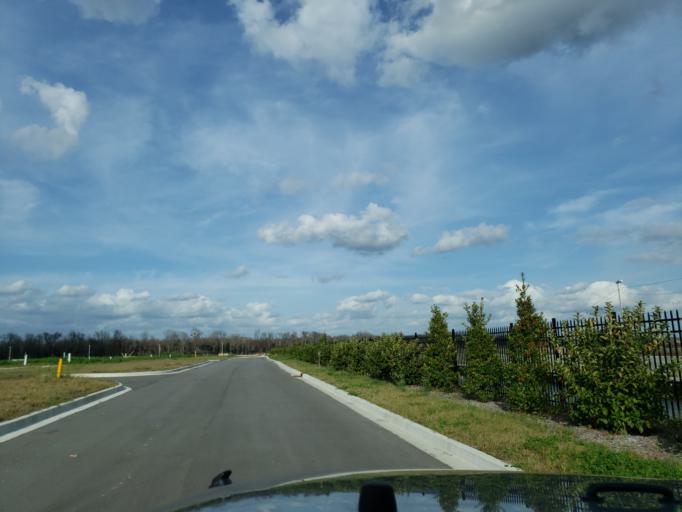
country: US
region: Georgia
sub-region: Chatham County
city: Savannah
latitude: 32.0763
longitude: -81.0747
